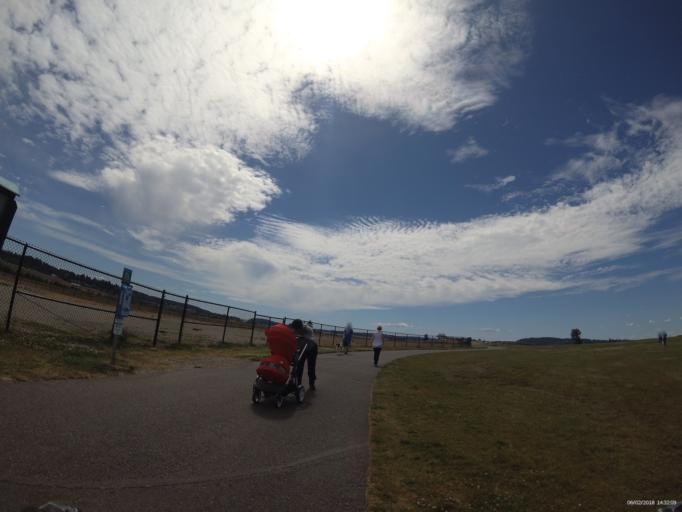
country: US
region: Washington
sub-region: Pierce County
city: Steilacoom
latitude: 47.2005
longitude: -122.5787
